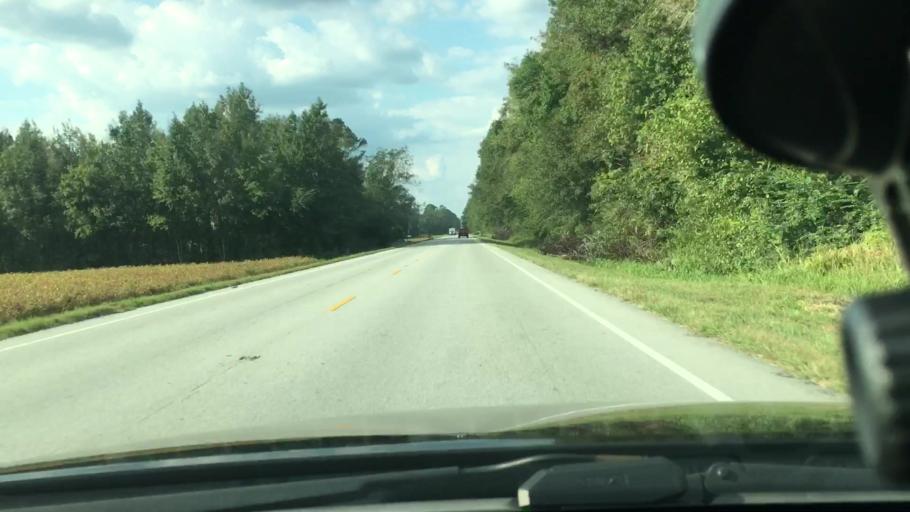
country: US
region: North Carolina
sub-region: Craven County
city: New Bern
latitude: 35.1720
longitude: -77.0436
